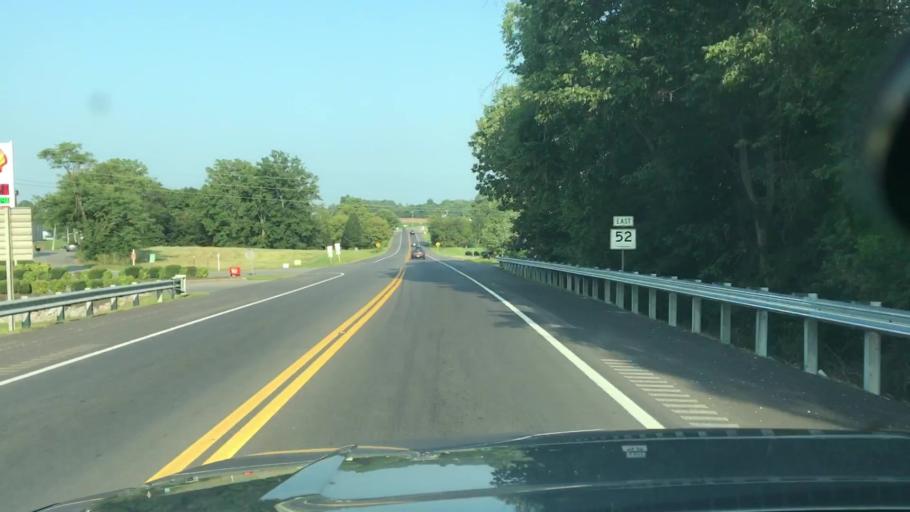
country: US
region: Tennessee
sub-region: Sumner County
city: Portland
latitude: 36.5914
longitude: -86.5984
